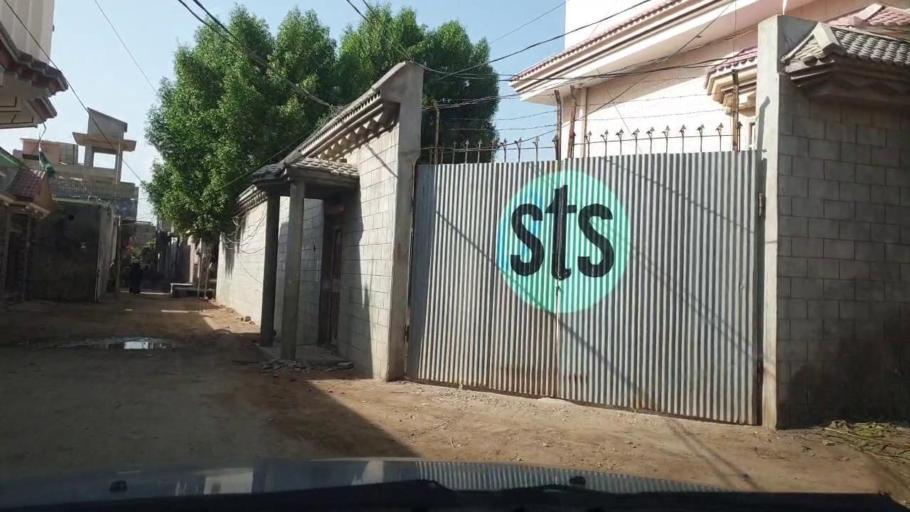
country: PK
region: Sindh
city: Matli
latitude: 25.0483
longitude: 68.6569
